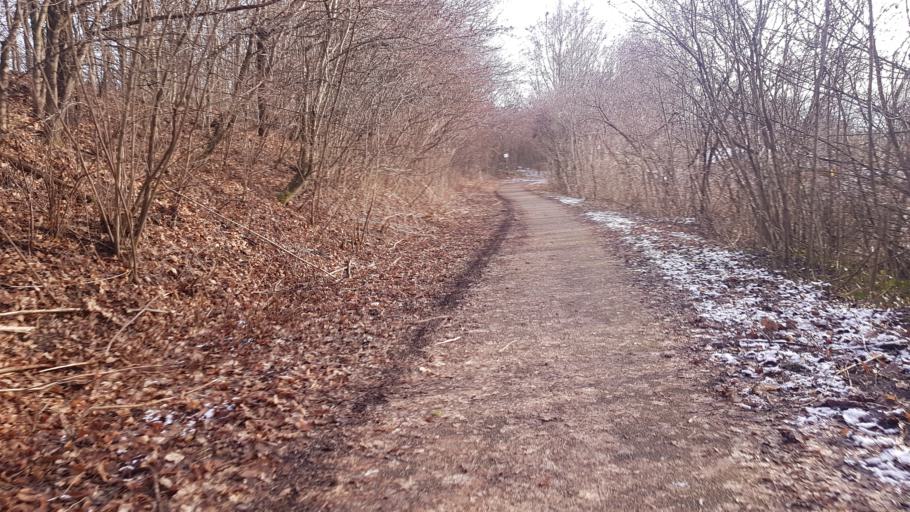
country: DE
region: Bavaria
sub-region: Upper Bavaria
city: Aschheim
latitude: 48.1441
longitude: 11.6928
